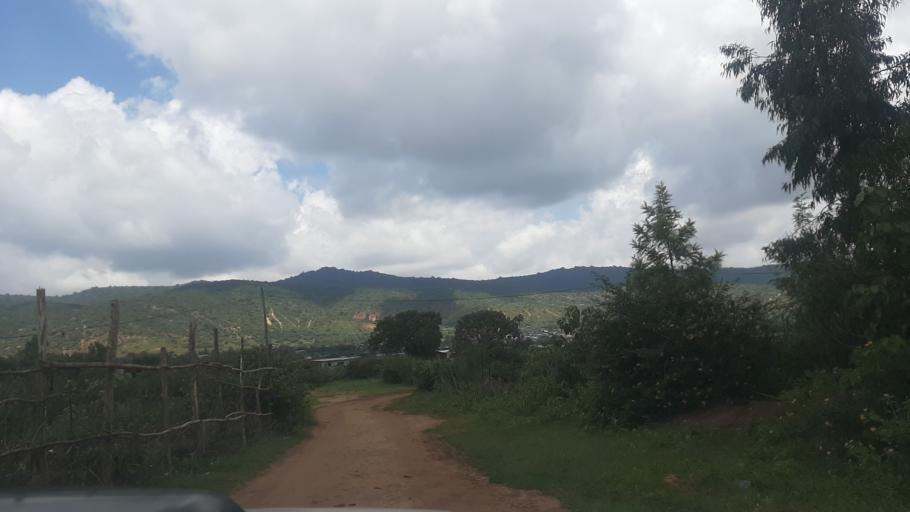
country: ET
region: Oromiya
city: Yabelo
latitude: 4.8922
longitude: 38.0823
